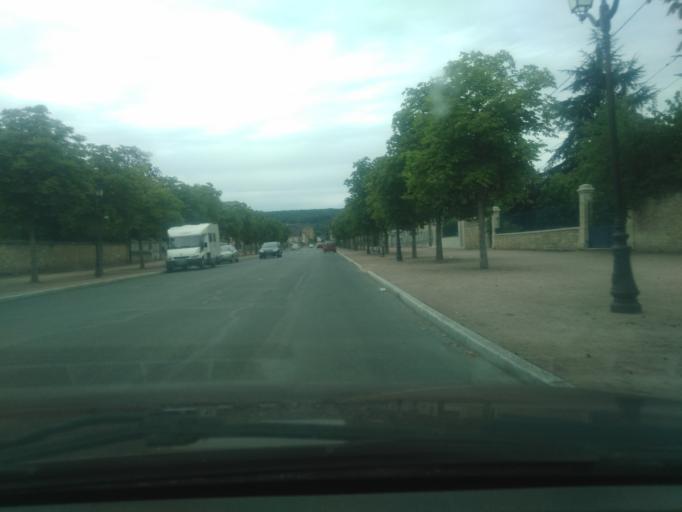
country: FR
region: Centre
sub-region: Departement du Cher
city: Saint-Amand-Montrond
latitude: 46.7258
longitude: 2.5071
